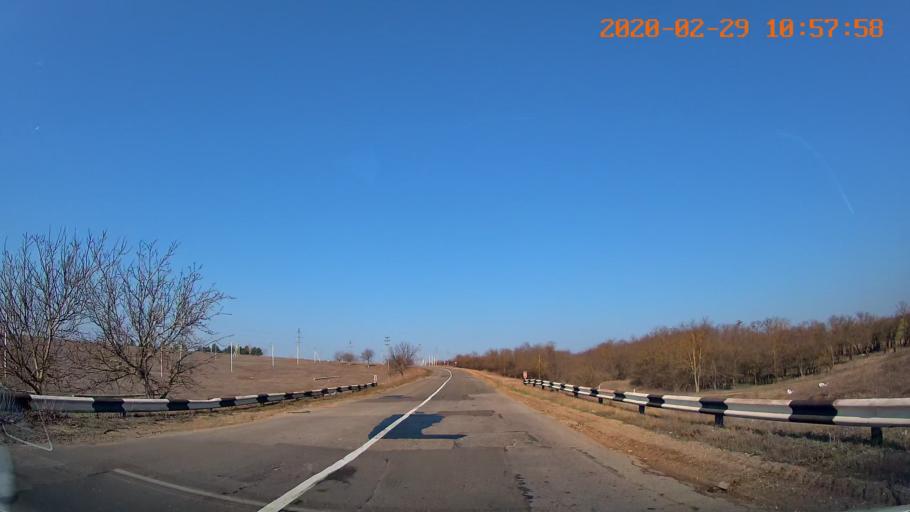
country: MD
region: Telenesti
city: Grigoriopol
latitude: 47.1654
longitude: 29.3184
